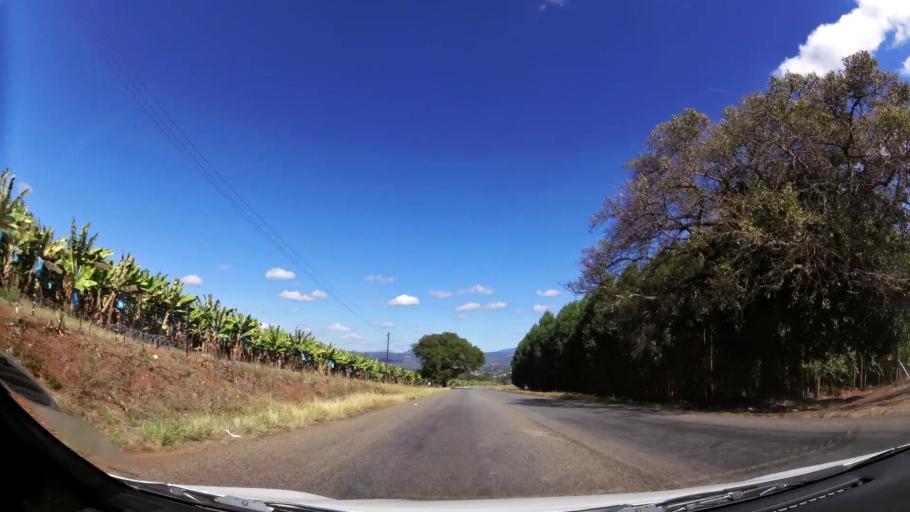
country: ZA
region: Limpopo
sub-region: Mopani District Municipality
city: Tzaneen
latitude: -23.8077
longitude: 30.1770
